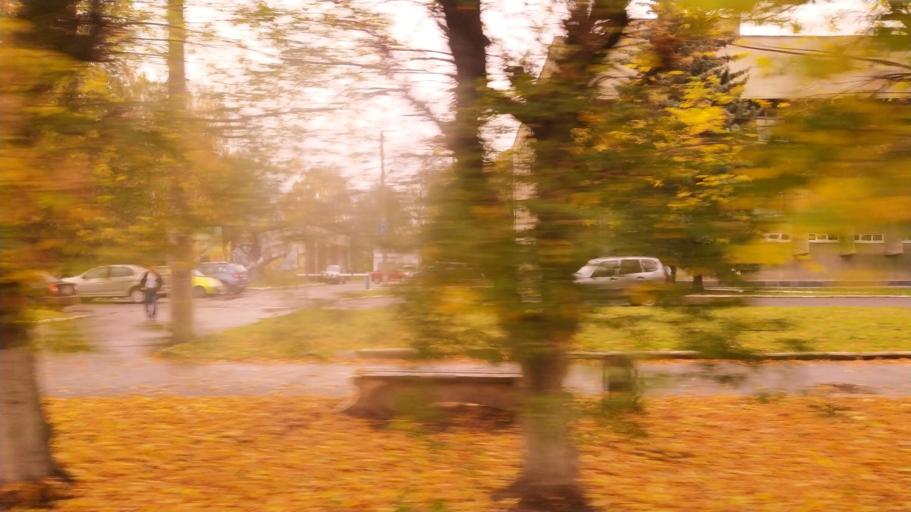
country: RU
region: Tverskaya
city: Tver
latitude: 56.8450
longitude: 35.9172
